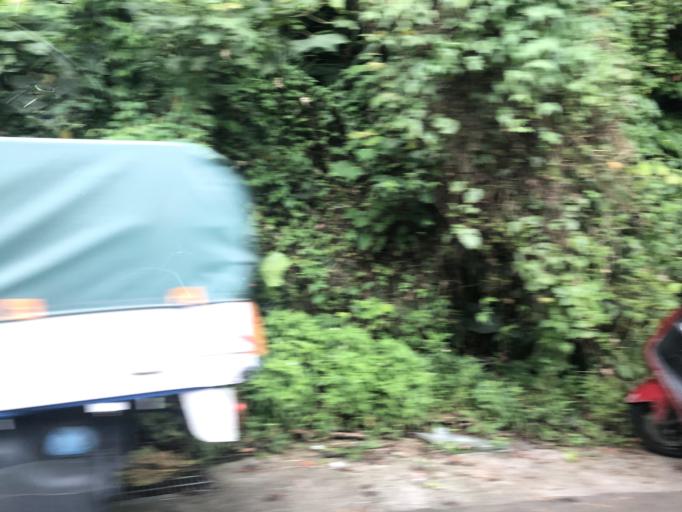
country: TW
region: Taiwan
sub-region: Taoyuan
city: Taoyuan
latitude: 24.9237
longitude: 121.3799
